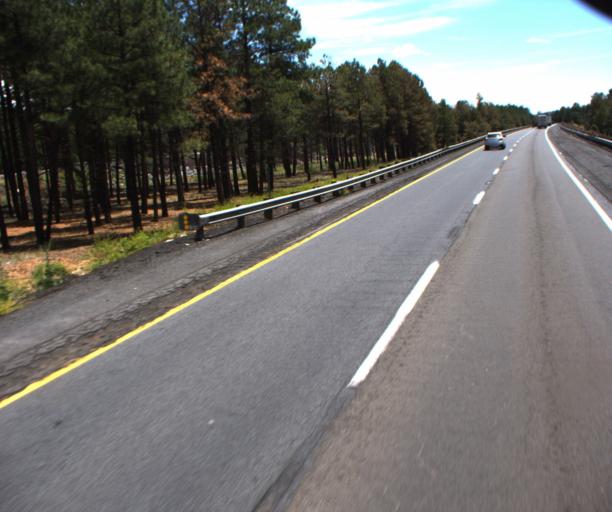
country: US
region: Arizona
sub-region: Coconino County
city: Flagstaff
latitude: 35.2206
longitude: -111.7920
